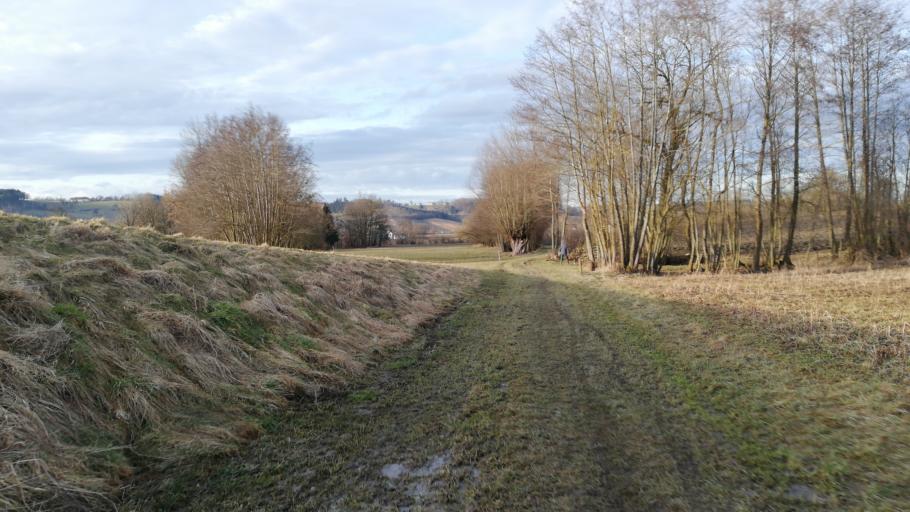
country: AT
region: Upper Austria
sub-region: Politischer Bezirk Grieskirchen
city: Bad Schallerbach
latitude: 48.1997
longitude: 13.9308
